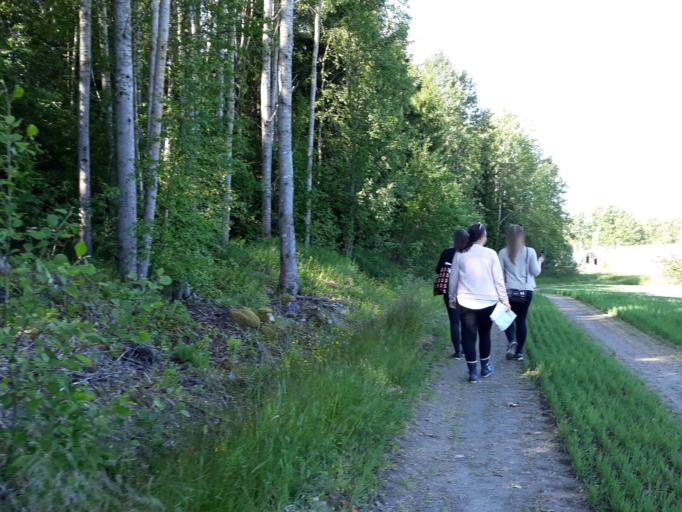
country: FI
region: Uusimaa
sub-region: Helsinki
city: Jaervenpaeae
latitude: 60.5394
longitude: 24.9824
